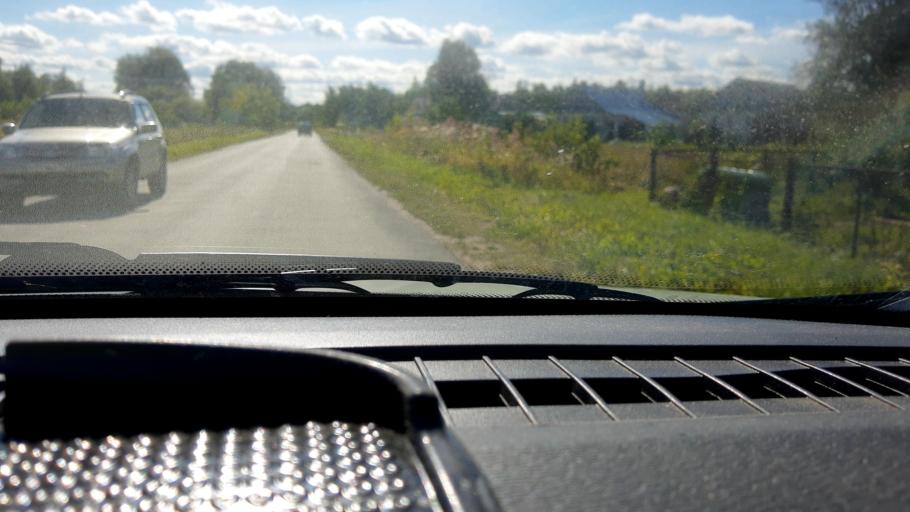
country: RU
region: Nizjnij Novgorod
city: Lukino
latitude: 56.4344
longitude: 43.6588
